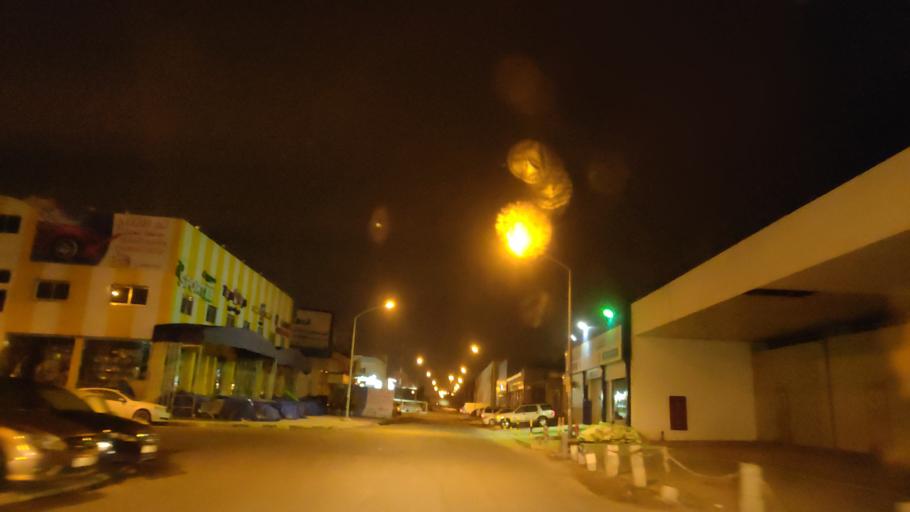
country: KW
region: Al Asimah
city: Ar Rabiyah
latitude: 29.3076
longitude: 47.9283
